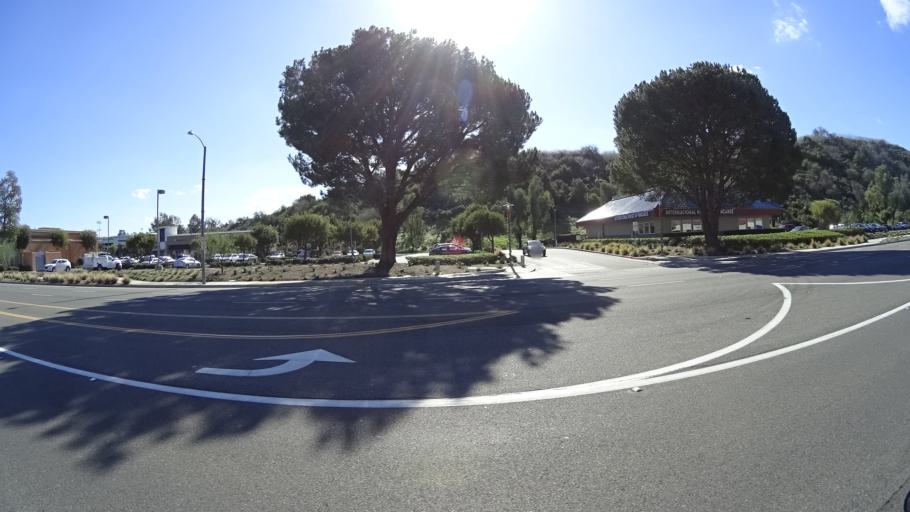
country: US
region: California
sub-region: Orange County
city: Aliso Viejo
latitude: 33.5562
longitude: -117.7153
